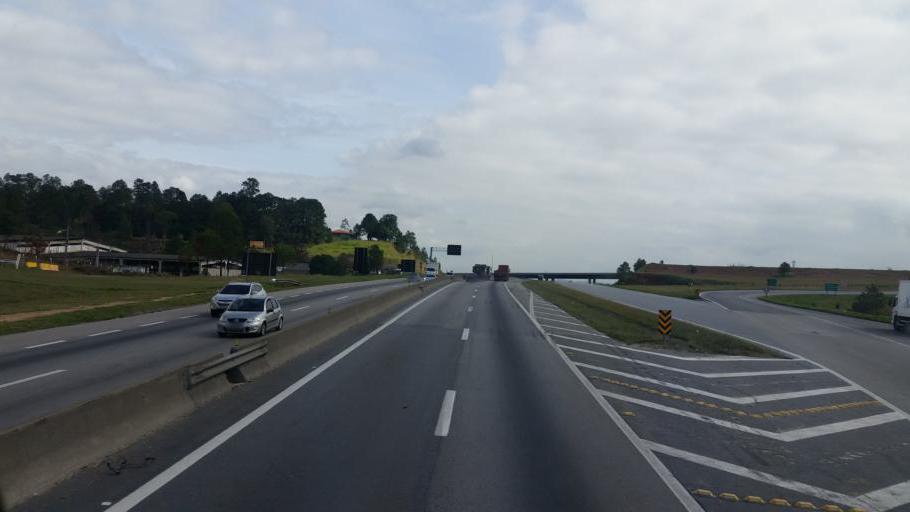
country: BR
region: Sao Paulo
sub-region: Jacarei
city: Jacarei
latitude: -23.3064
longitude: -46.0388
